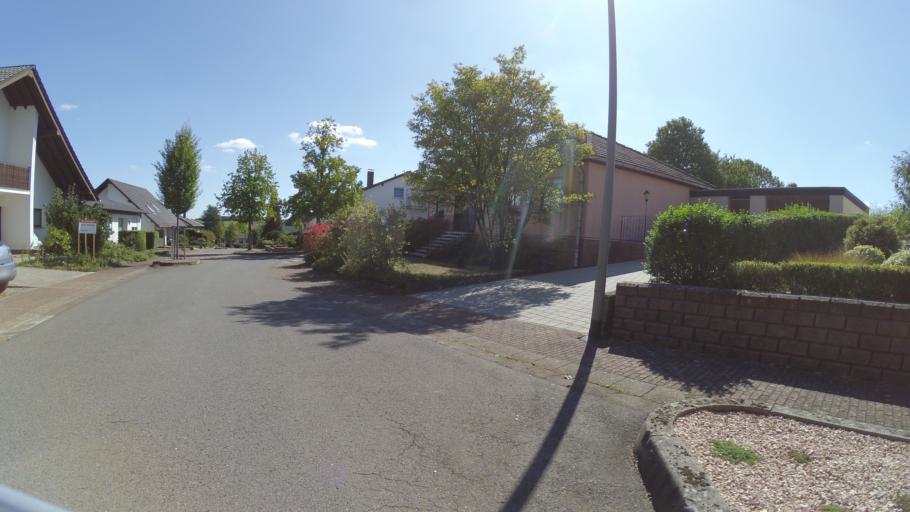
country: DE
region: Saarland
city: Lebach
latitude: 49.3894
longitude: 6.9008
